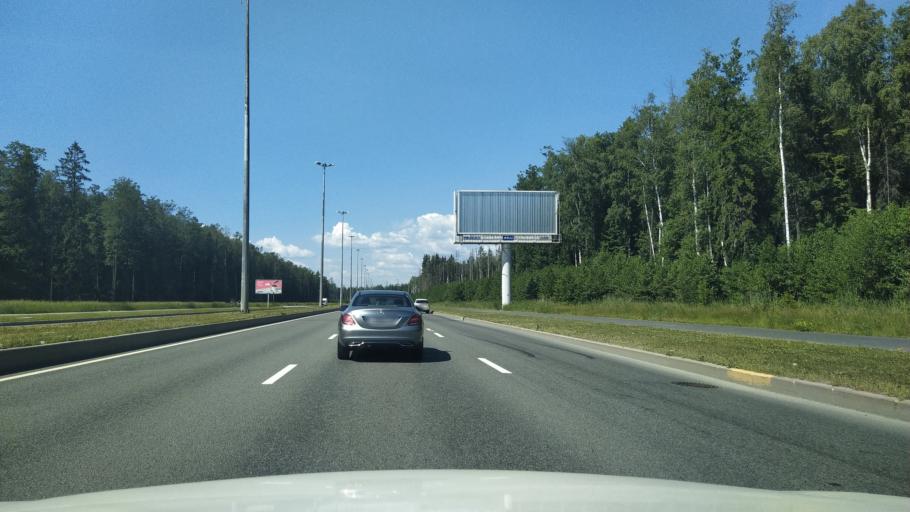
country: RU
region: Leningrad
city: Untolovo
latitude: 60.0566
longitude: 30.2227
